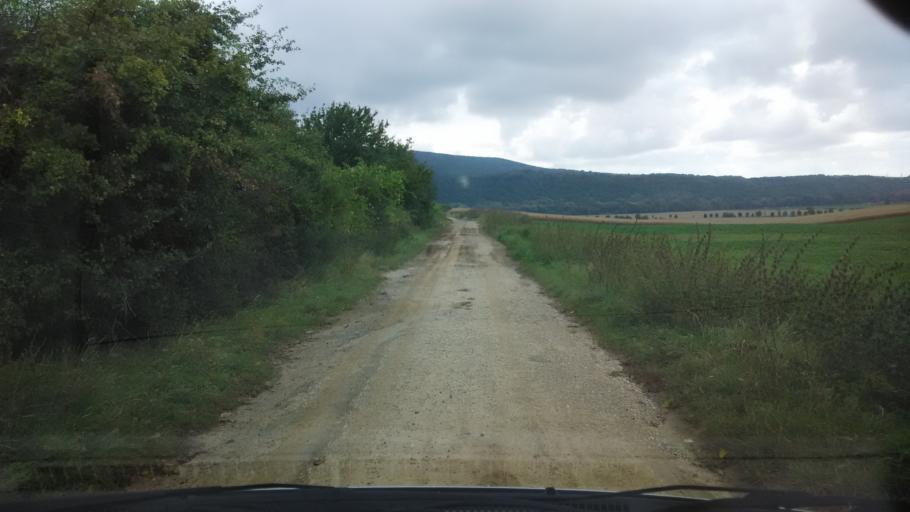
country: SK
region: Nitriansky
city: Tlmace
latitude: 48.3328
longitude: 18.5352
